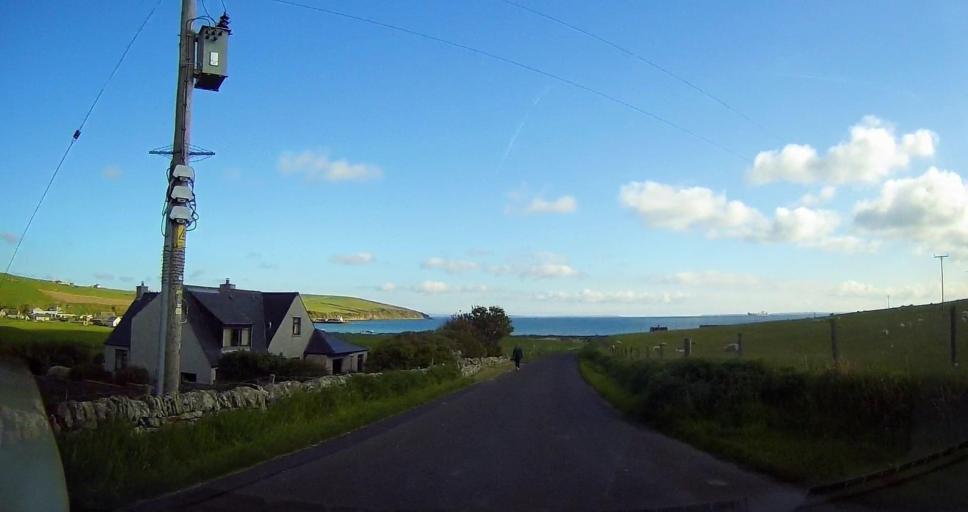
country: GB
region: Scotland
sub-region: Orkney Islands
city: Orkney
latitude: 58.9656
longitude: -2.9773
